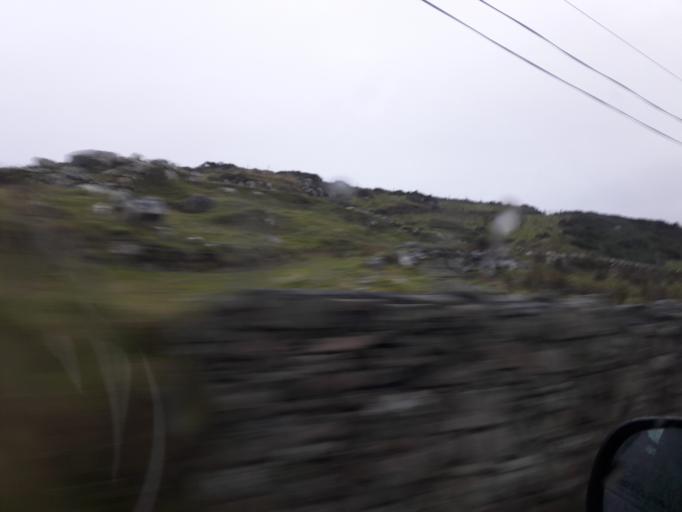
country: IE
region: Ulster
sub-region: County Donegal
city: Ramelton
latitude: 55.2635
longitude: -7.6624
